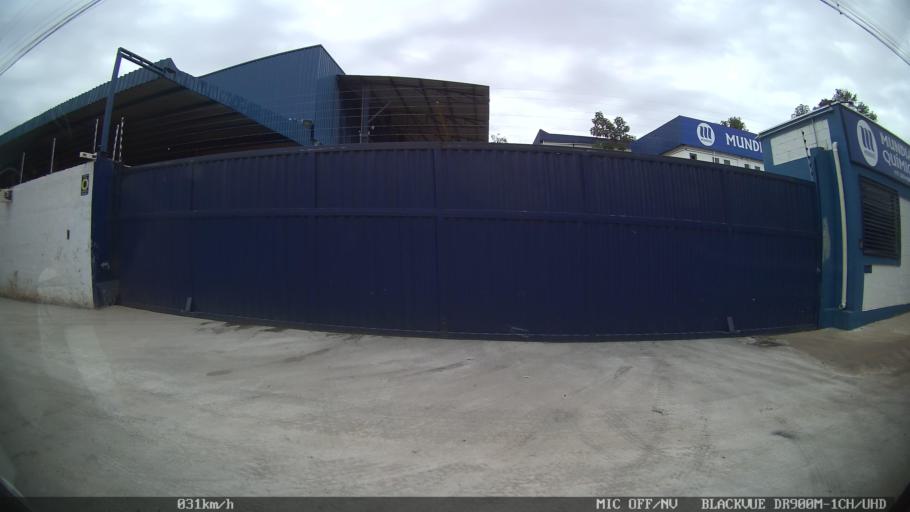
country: BR
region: Sao Paulo
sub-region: Sao Jose Do Rio Preto
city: Sao Jose do Rio Preto
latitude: -20.8200
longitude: -49.4294
